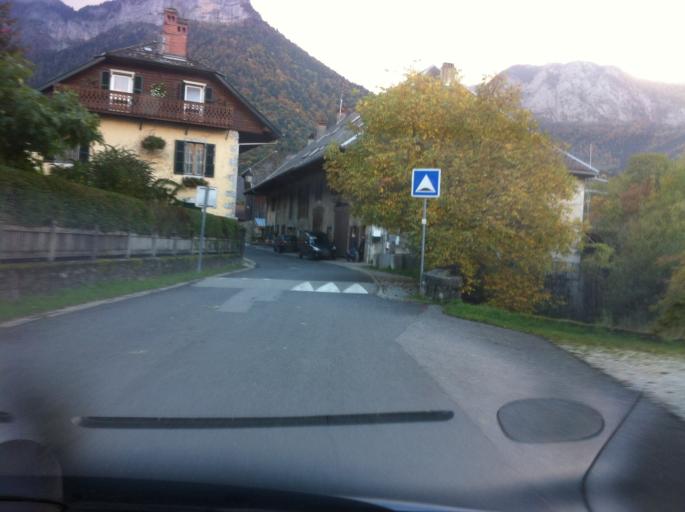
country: FR
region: Rhone-Alpes
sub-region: Departement de la Haute-Savoie
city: Doussard
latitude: 45.7693
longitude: 6.2239
